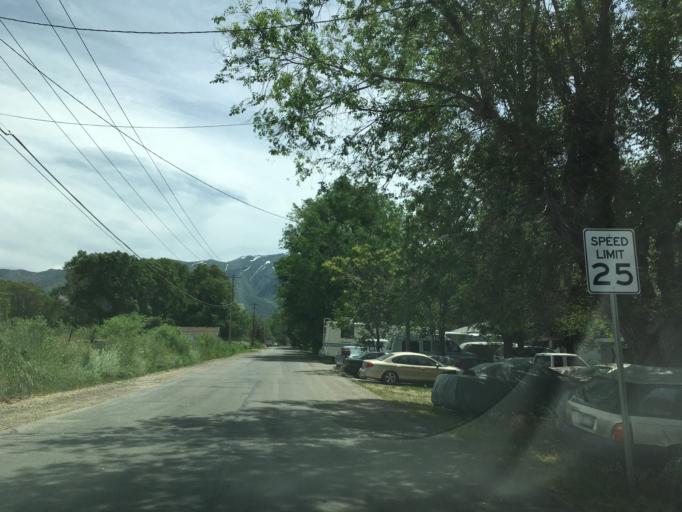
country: US
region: Utah
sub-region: Davis County
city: Hill Air Force Bace
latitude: 41.0988
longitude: -111.9592
